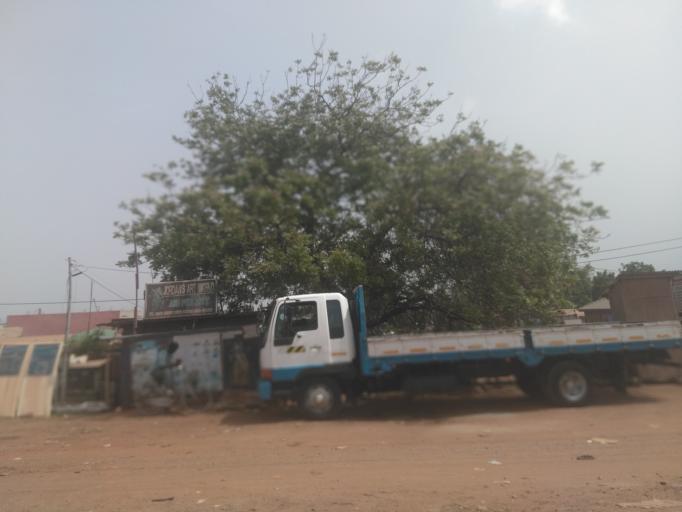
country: GH
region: Greater Accra
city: Tema
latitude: 5.6956
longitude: -0.0137
